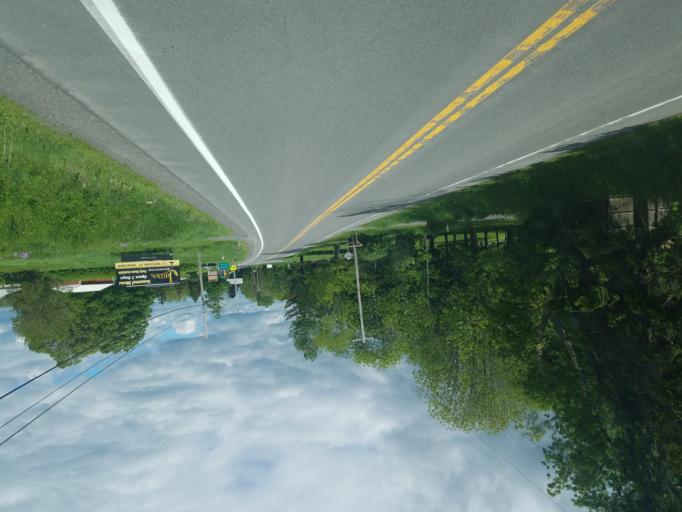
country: US
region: New York
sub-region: Herkimer County
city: Mohawk
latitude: 42.9594
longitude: -75.0156
